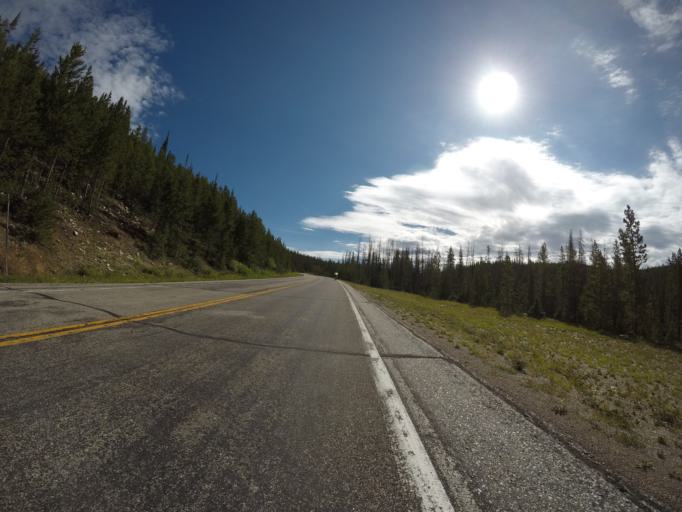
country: US
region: Wyoming
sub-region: Carbon County
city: Saratoga
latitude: 41.3245
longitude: -106.4463
